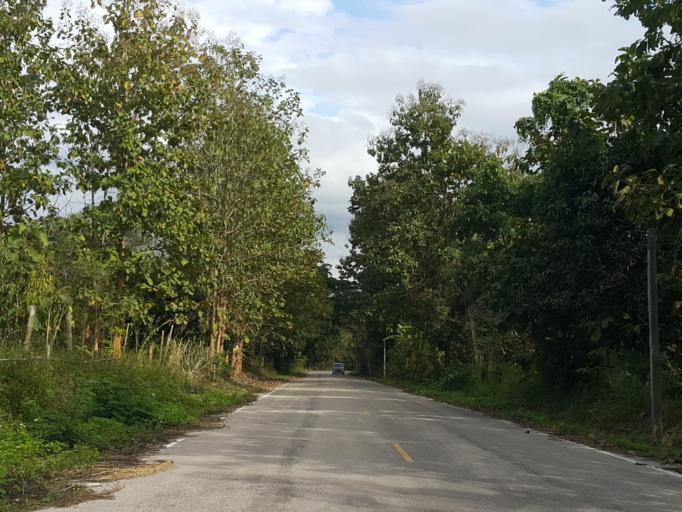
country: TH
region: Lampang
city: Chae Hom
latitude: 18.6532
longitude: 99.5329
